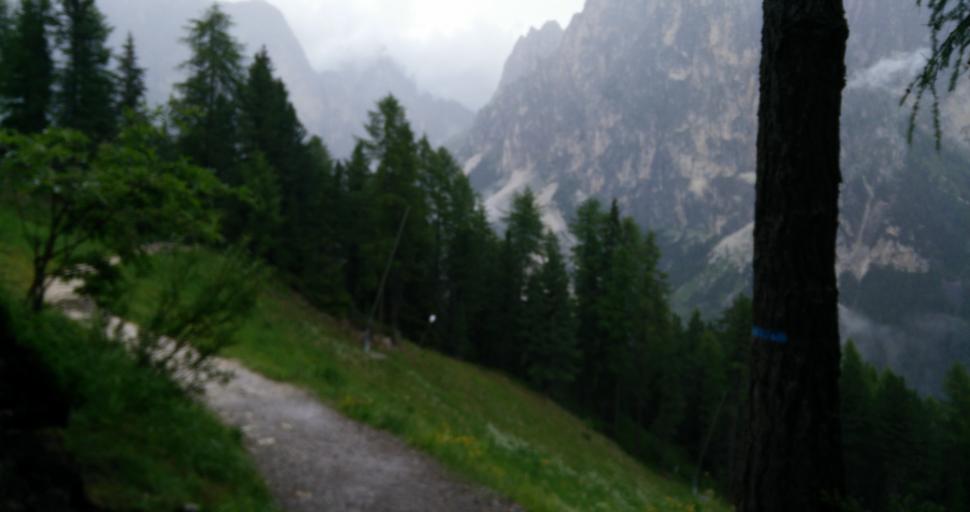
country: IT
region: Trentino-Alto Adige
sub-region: Provincia di Trento
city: Vigo di Fassa
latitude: 46.4355
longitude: 11.6572
